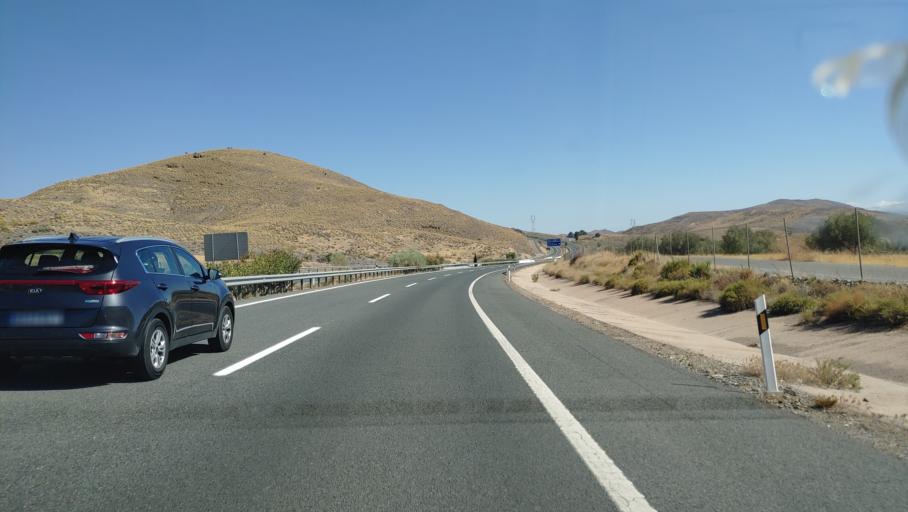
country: ES
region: Andalusia
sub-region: Provincia de Almeria
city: Gergal
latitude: 37.1348
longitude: -2.6433
